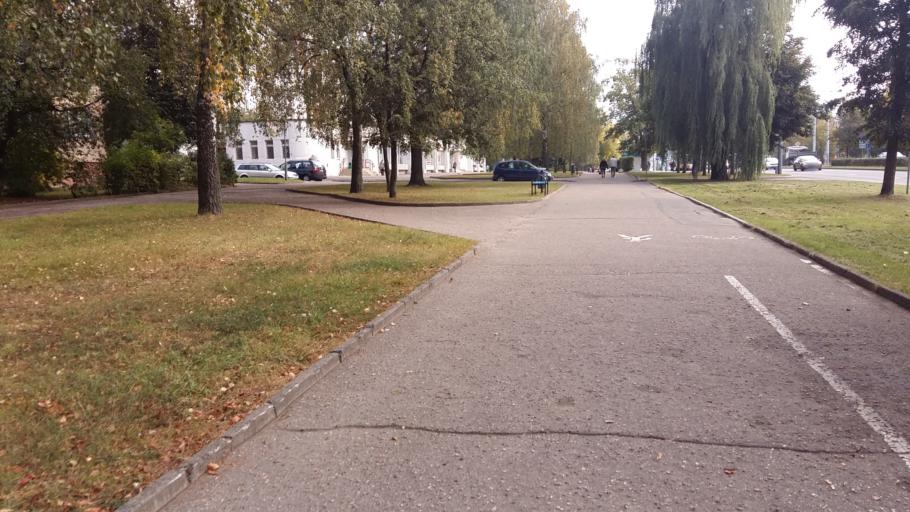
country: BY
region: Grodnenskaya
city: Hrodna
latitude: 53.6979
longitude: 23.8059
